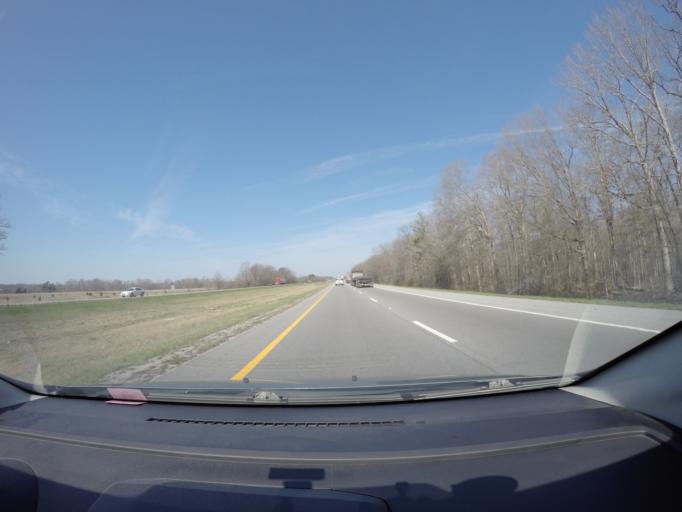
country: US
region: Tennessee
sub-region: Coffee County
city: New Union
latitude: 35.5286
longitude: -86.1464
